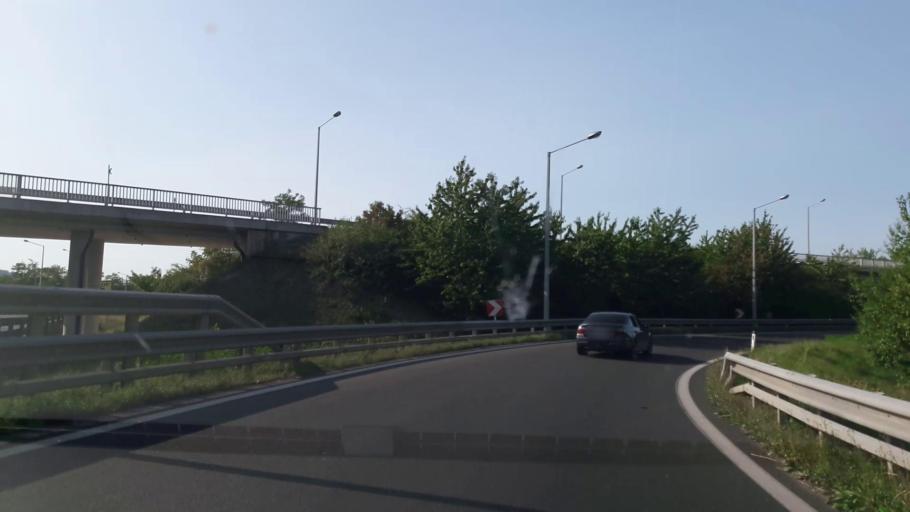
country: AT
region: Lower Austria
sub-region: Politischer Bezirk Modling
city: Brunn am Gebirge
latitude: 48.1157
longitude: 16.2952
